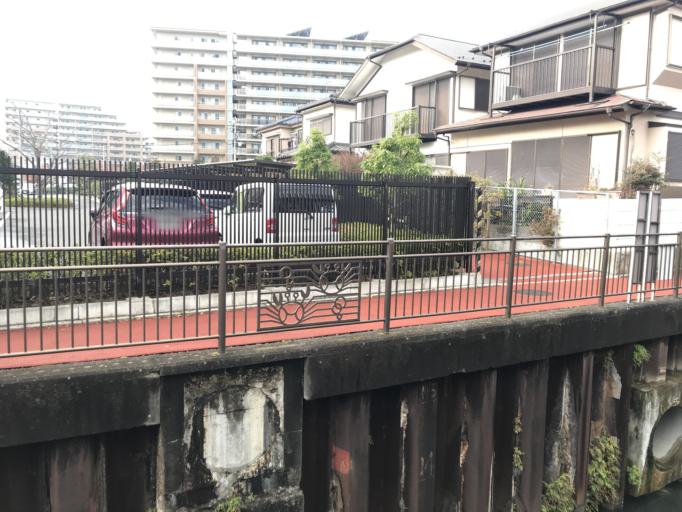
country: JP
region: Chiba
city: Funabashi
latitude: 35.7112
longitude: 139.9842
